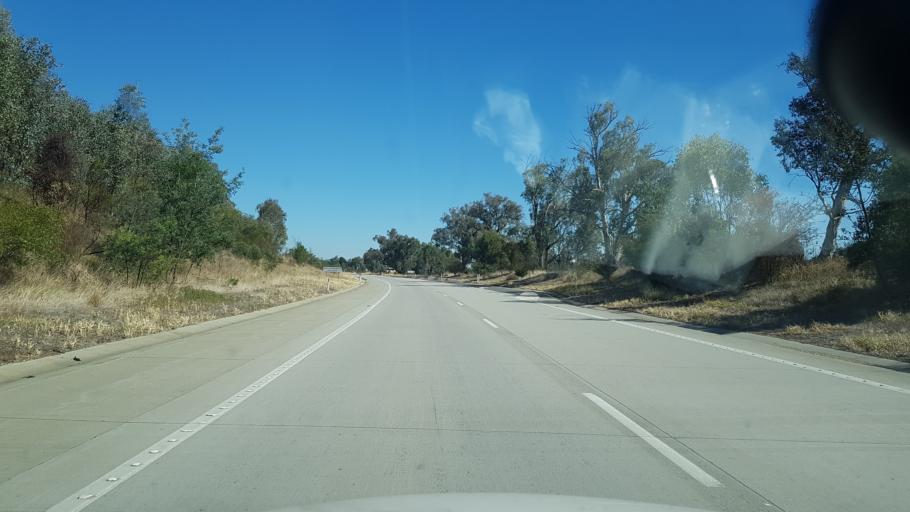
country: AU
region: New South Wales
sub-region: Greater Hume Shire
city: Holbrook
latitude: -35.8948
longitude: 147.1687
